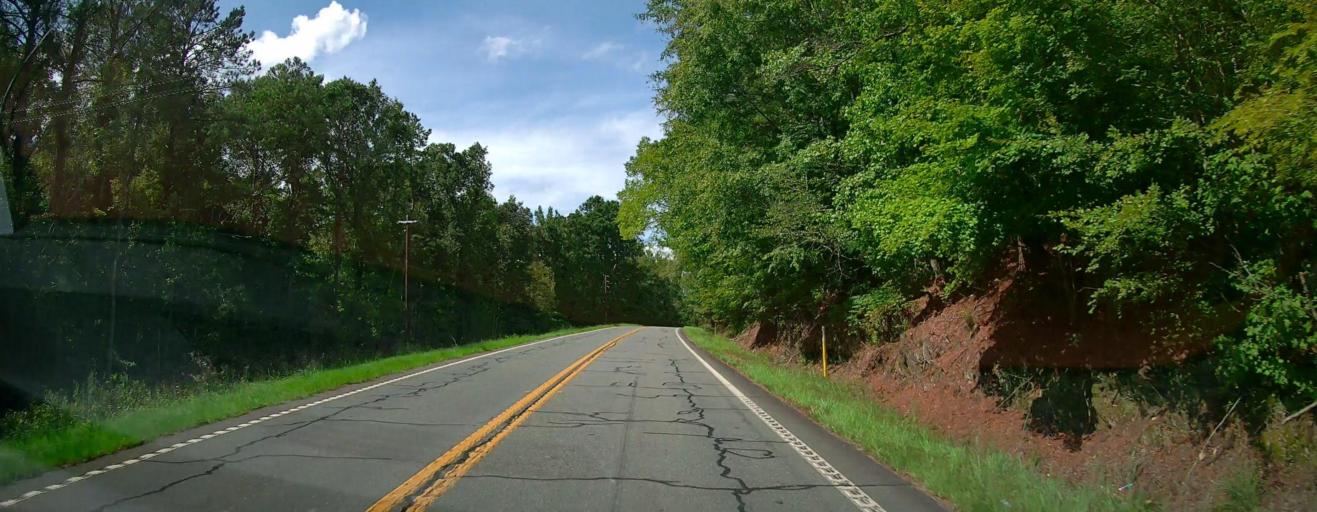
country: US
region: Georgia
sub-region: Talbot County
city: Talbotton
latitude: 32.7000
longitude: -84.5511
